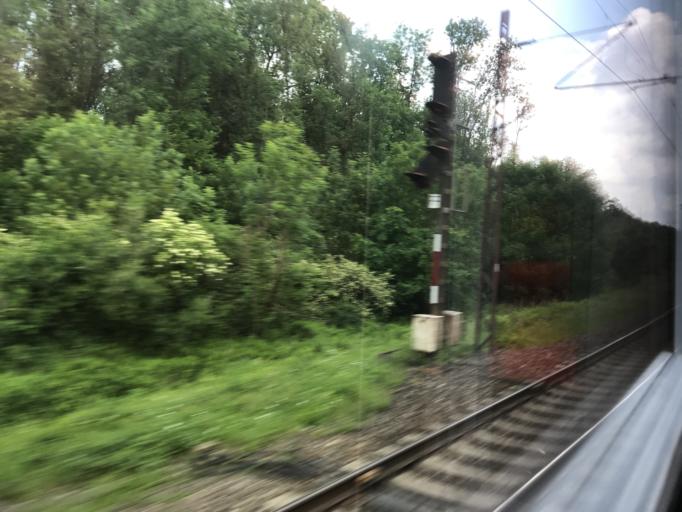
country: DE
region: Bavaria
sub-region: Swabia
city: Guenzburg
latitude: 48.4580
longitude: 10.2663
